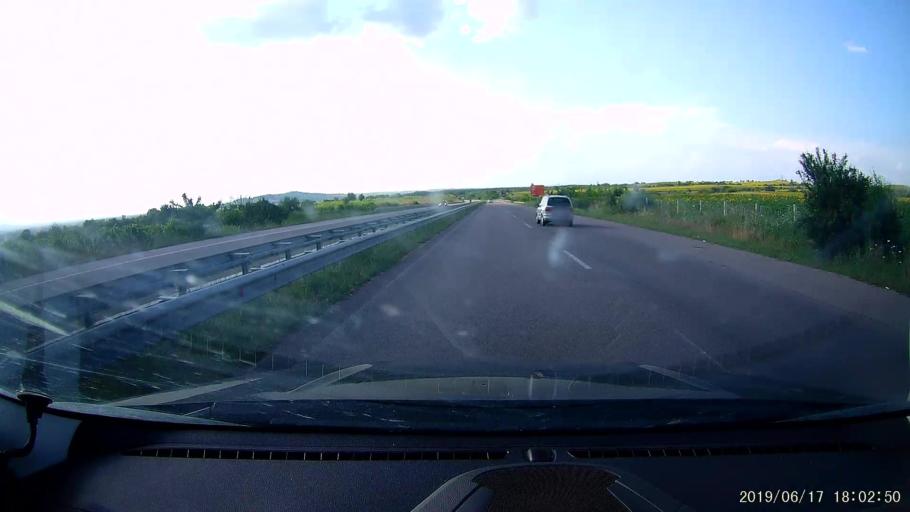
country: BG
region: Khaskovo
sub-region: Obshtina Svilengrad
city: Svilengrad
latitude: 41.7669
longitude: 26.2264
